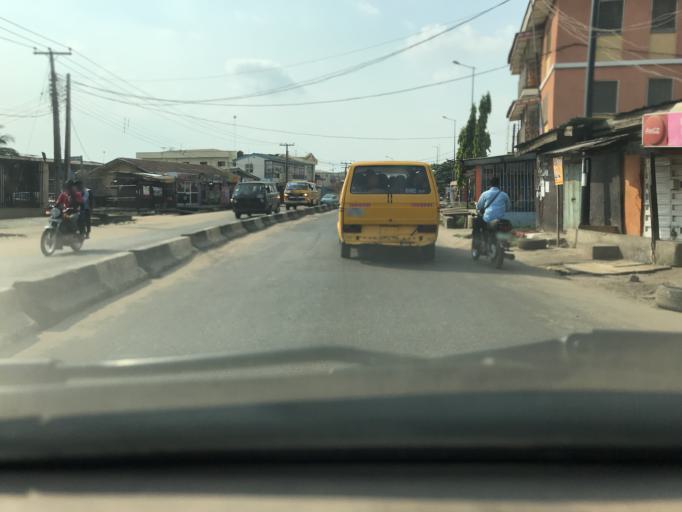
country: NG
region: Lagos
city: Agege
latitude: 6.6000
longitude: 3.2987
